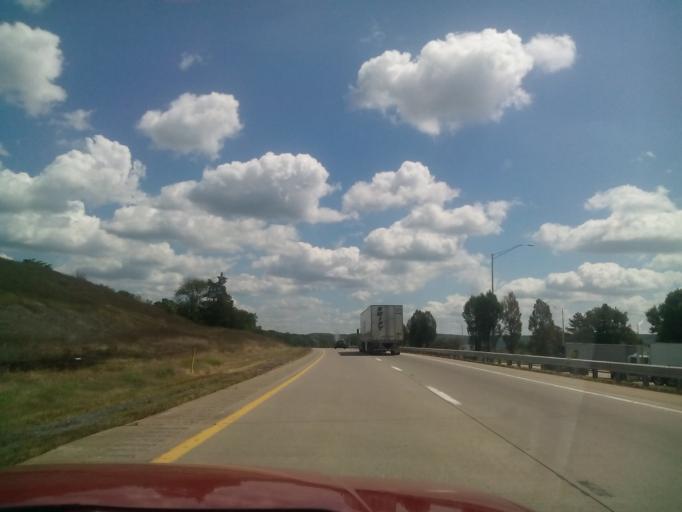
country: US
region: Pennsylvania
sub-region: Northumberland County
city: Milton
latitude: 40.9916
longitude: -76.7397
